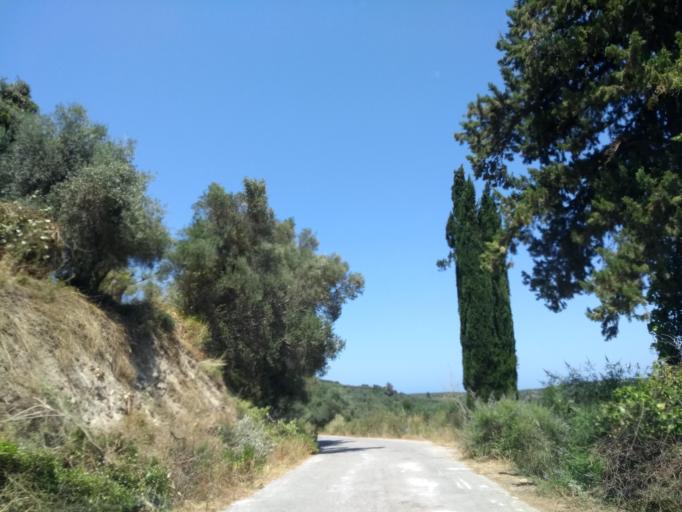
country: GR
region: Crete
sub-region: Nomos Chanias
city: Georgioupolis
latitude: 35.3229
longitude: 24.3136
